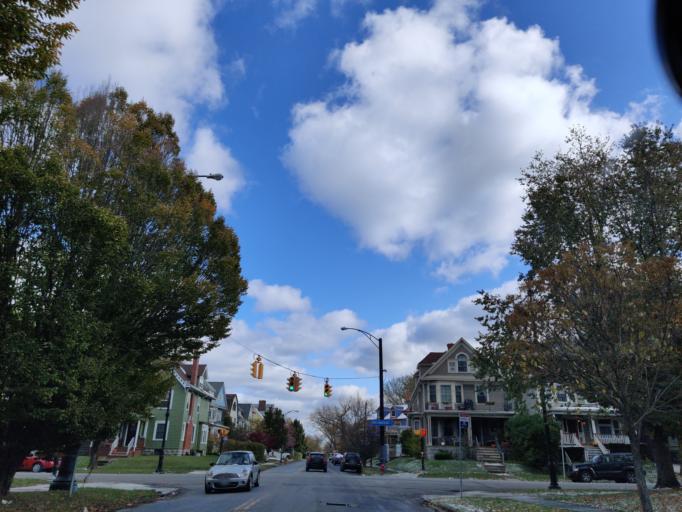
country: US
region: New York
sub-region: Erie County
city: Buffalo
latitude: 42.9221
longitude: -78.8818
